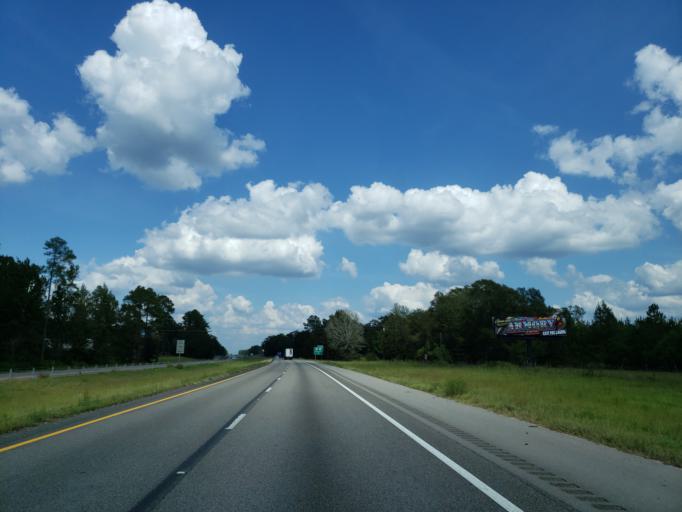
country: US
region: Mississippi
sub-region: Jones County
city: Ellisville
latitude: 31.5999
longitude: -89.2210
